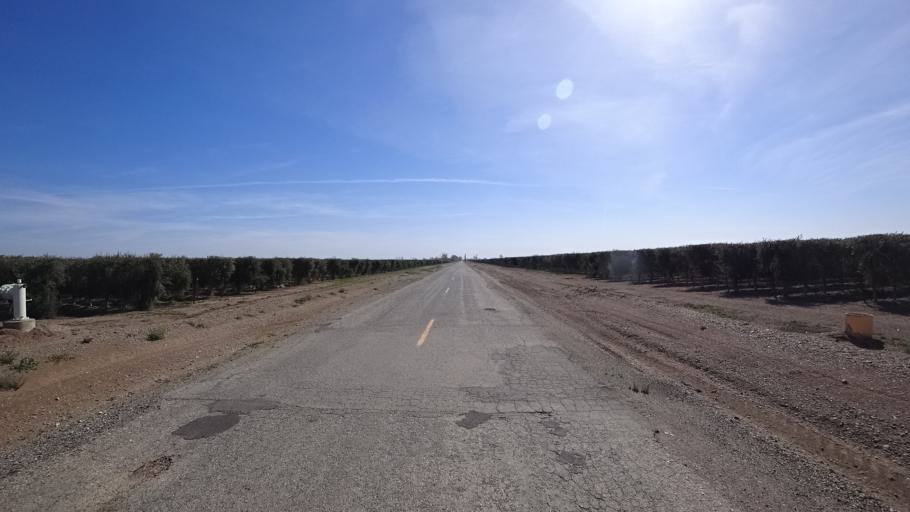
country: US
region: California
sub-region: Glenn County
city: Willows
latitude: 39.6116
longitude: -122.2571
